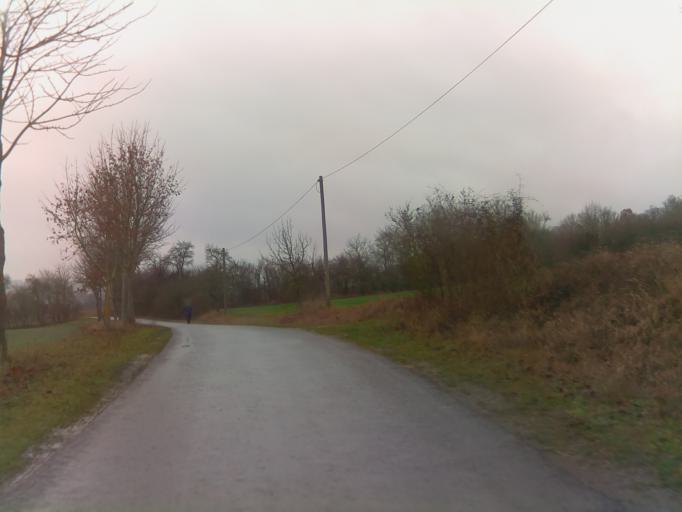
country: DE
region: Thuringia
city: Romhild
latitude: 50.4157
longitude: 10.5588
